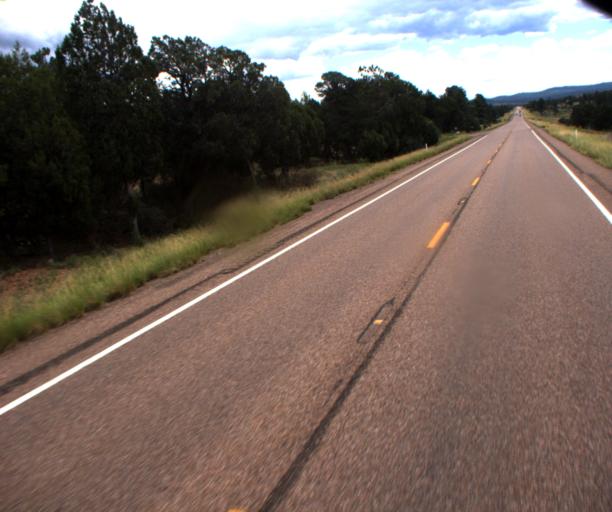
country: US
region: Arizona
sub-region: Navajo County
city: Linden
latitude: 34.3333
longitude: -110.2687
